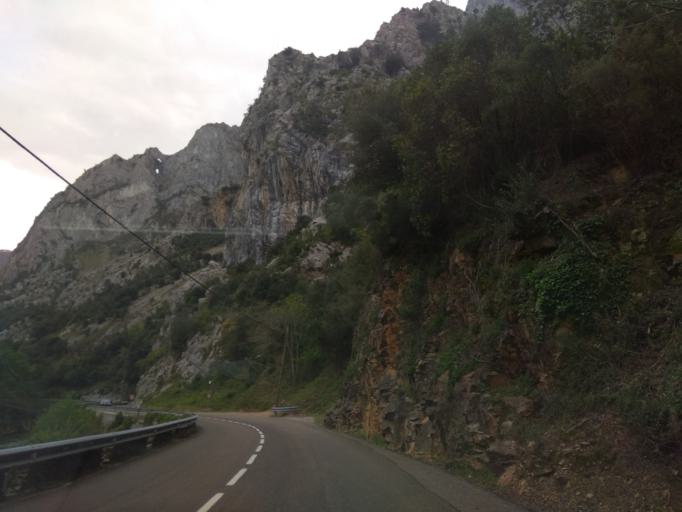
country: ES
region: Cantabria
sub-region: Provincia de Cantabria
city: Tresviso
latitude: 43.2756
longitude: -4.6367
